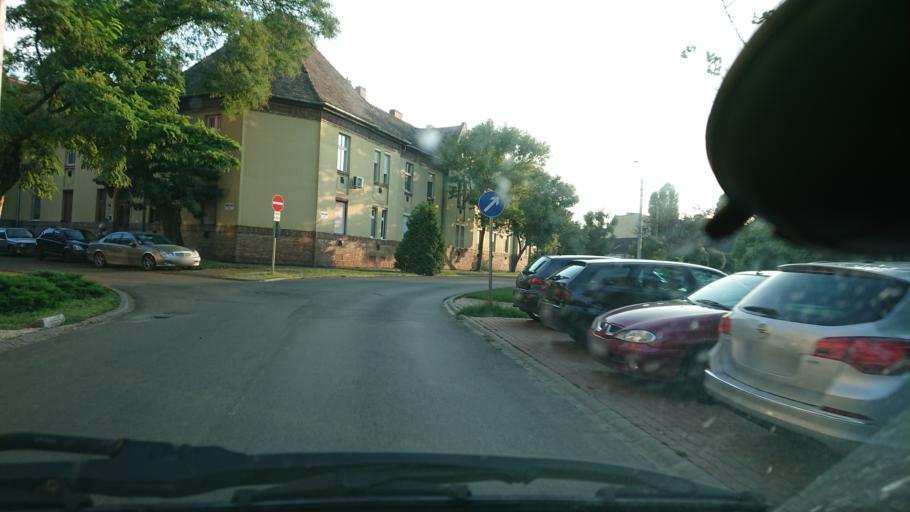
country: HU
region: Csongrad
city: Szeged
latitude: 46.2642
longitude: 20.1460
